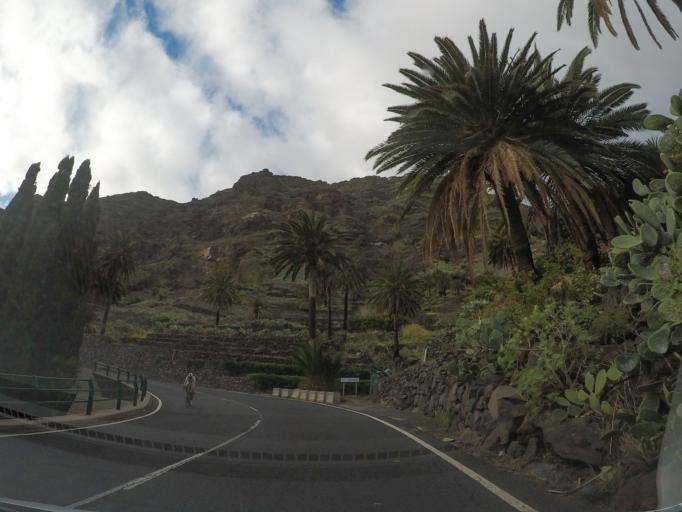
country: ES
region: Canary Islands
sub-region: Provincia de Santa Cruz de Tenerife
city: Vallehermosa
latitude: 28.1154
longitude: -17.3127
